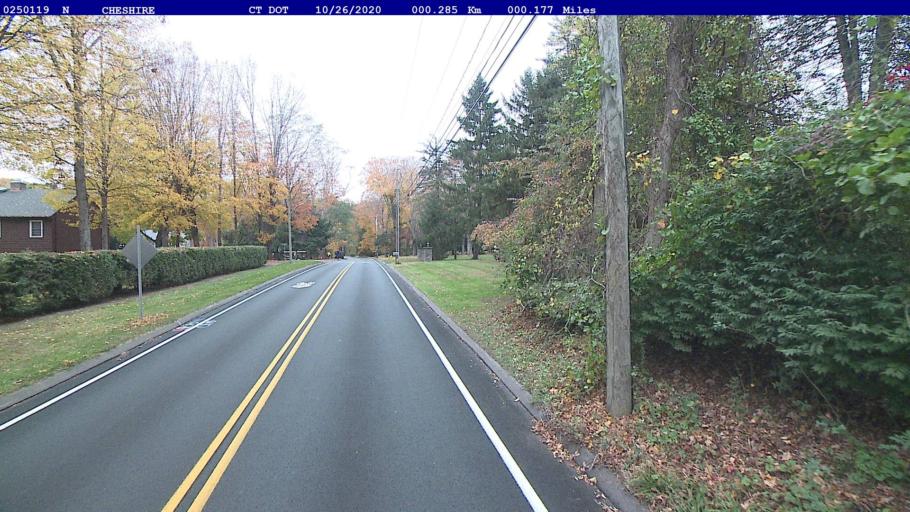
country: US
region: Connecticut
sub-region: New Haven County
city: Cheshire
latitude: 41.4802
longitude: -72.9300
